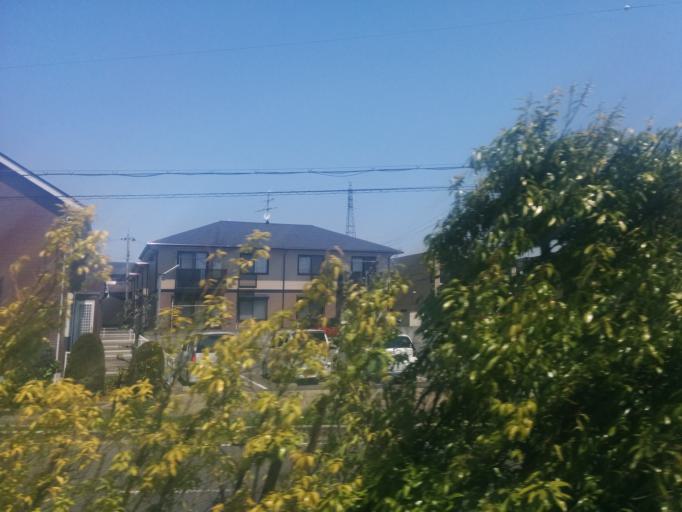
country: JP
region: Nara
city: Kashihara-shi
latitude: 34.5183
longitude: 135.7827
